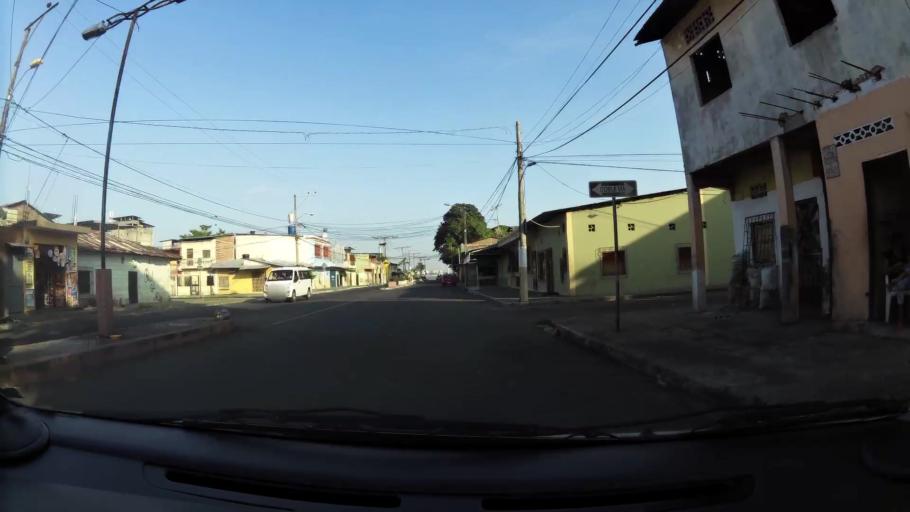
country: EC
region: Guayas
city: Eloy Alfaro
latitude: -2.1681
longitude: -79.8502
